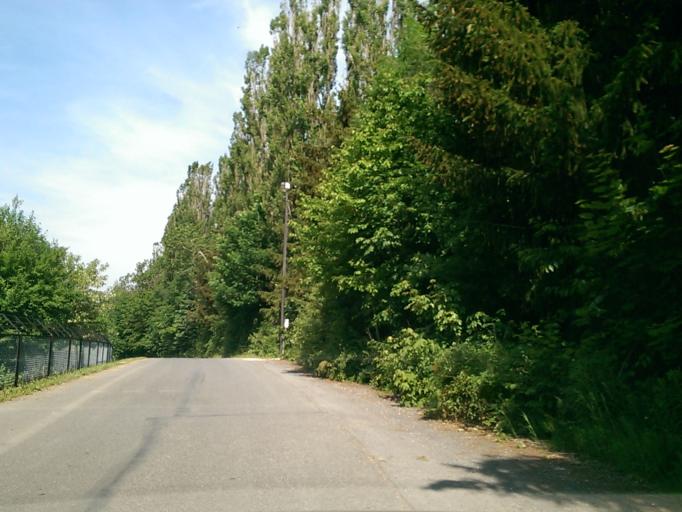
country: CZ
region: Kralovehradecky
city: Dvur Kralove nad Labem
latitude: 50.4336
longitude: 15.7881
